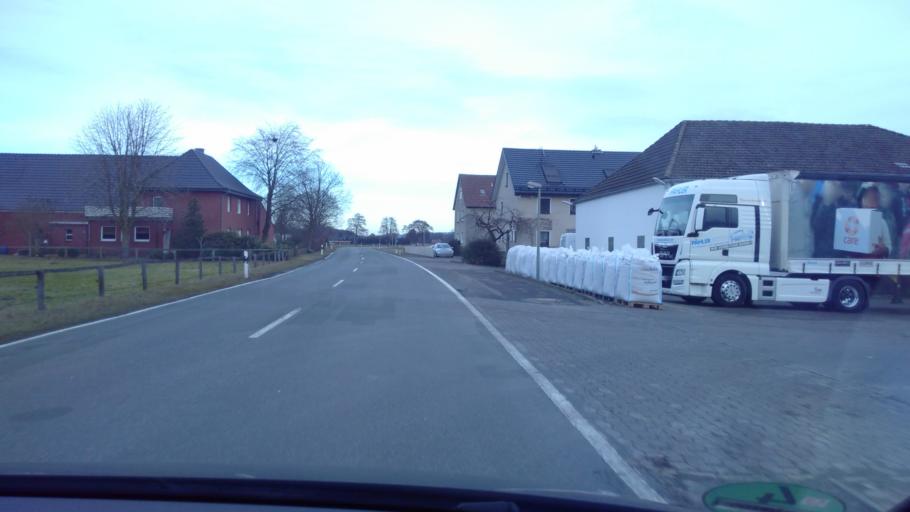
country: DE
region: North Rhine-Westphalia
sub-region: Regierungsbezirk Detmold
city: Verl
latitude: 51.8940
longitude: 8.5112
